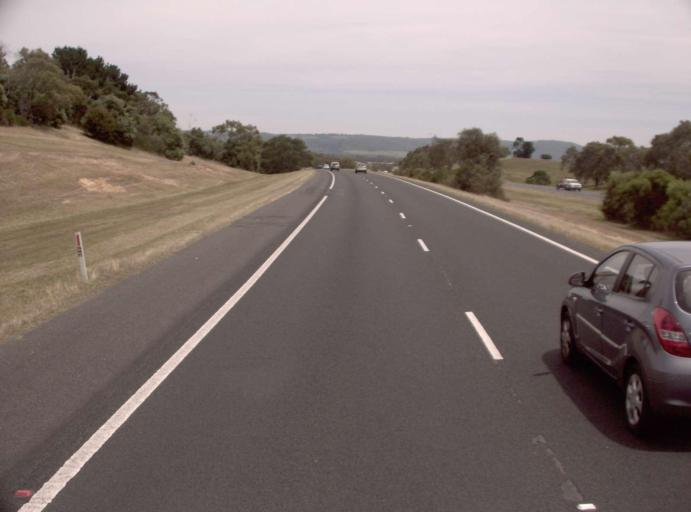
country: AU
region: Victoria
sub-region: Mornington Peninsula
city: Mount Martha
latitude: -38.2924
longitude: 145.0421
